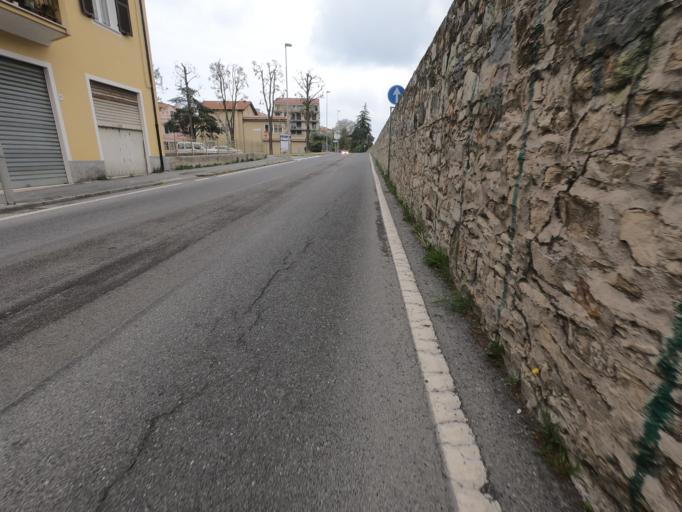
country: IT
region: Liguria
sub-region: Provincia di Savona
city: Andora
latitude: 43.9540
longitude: 8.1390
